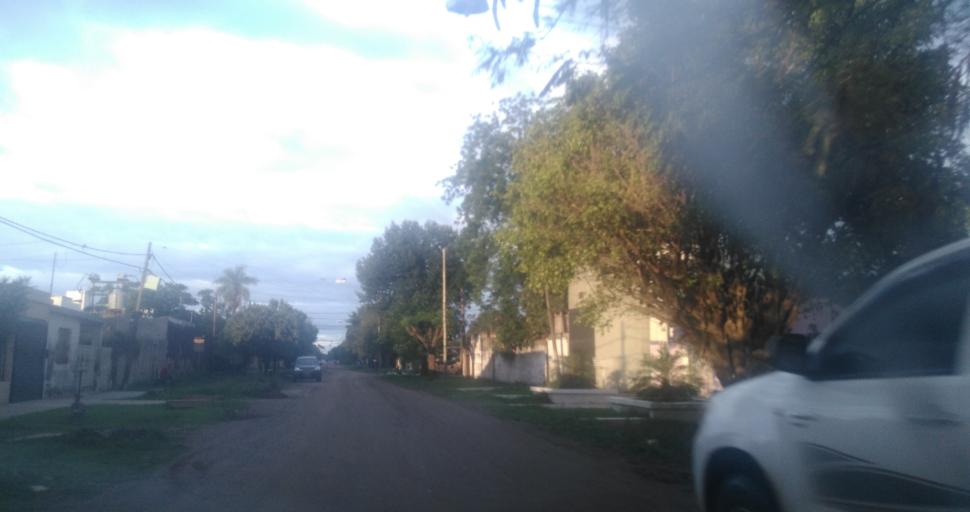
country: AR
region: Chaco
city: Resistencia
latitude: -27.4685
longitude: -58.9734
